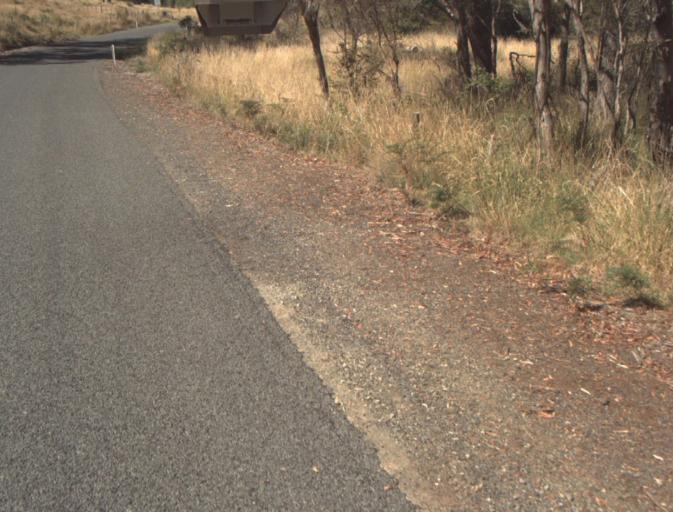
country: AU
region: Tasmania
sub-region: Launceston
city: Newstead
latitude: -41.3645
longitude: 147.3050
